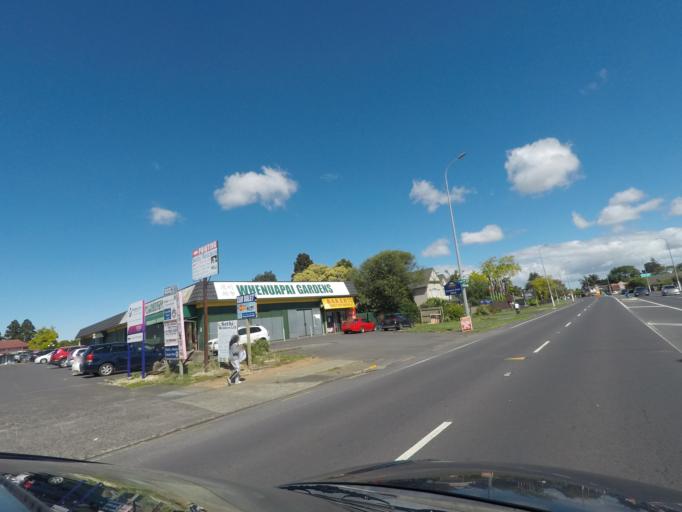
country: NZ
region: Auckland
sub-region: Auckland
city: Manukau City
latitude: -36.9806
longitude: 174.8764
